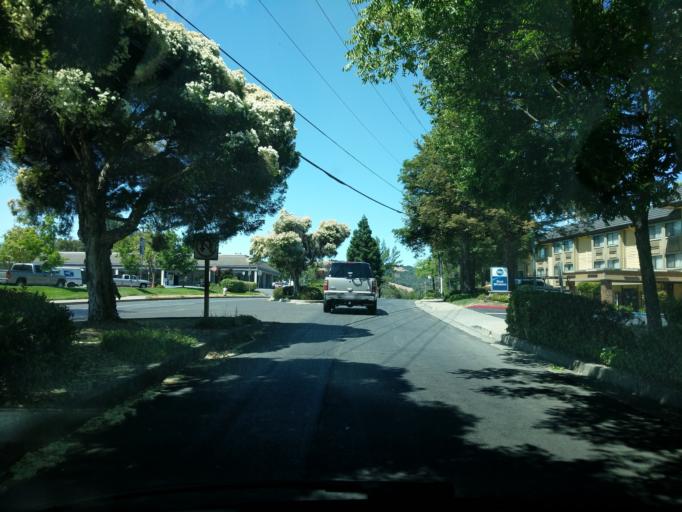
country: US
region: California
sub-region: Contra Costa County
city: Mountain View
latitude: 37.9936
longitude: -122.1200
